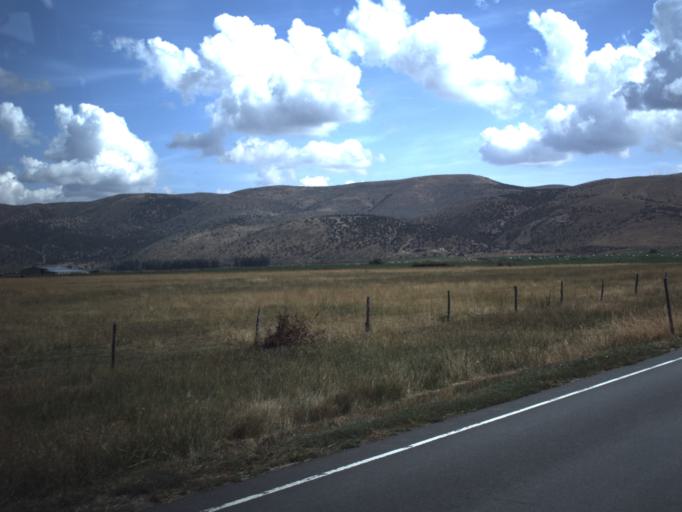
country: US
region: Utah
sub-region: Rich County
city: Randolph
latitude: 41.8349
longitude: -111.3304
